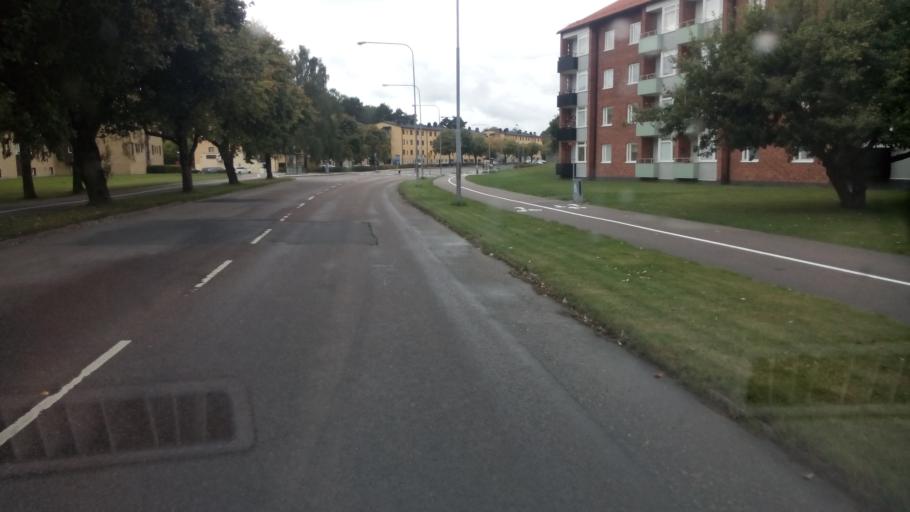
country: SE
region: Soedermanland
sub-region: Nykopings Kommun
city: Nykoping
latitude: 58.7545
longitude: 17.0342
